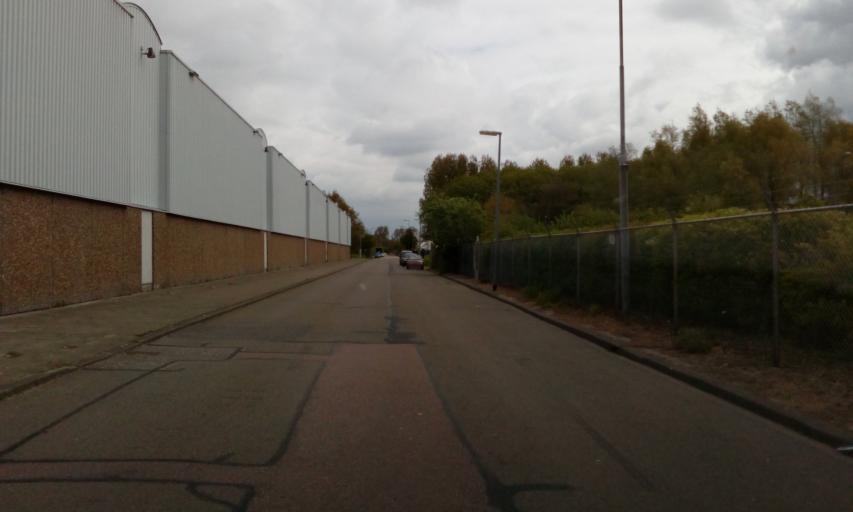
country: NL
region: South Holland
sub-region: Gemeente Rotterdam
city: Rotterdam
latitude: 51.9558
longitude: 4.4531
